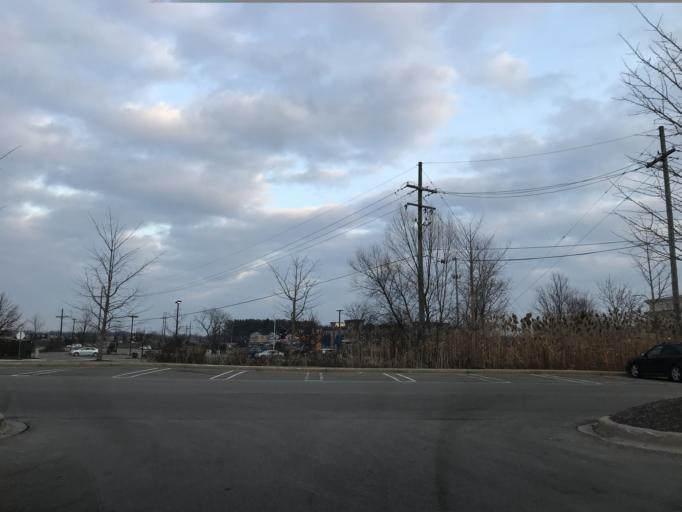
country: US
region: Michigan
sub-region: Livingston County
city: Brighton
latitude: 42.5035
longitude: -83.7607
